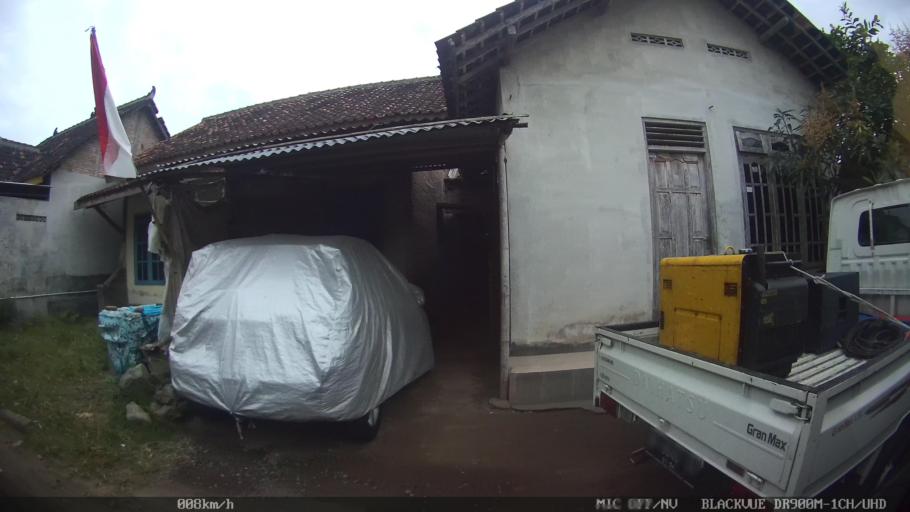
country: ID
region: Daerah Istimewa Yogyakarta
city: Sewon
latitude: -7.8328
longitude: 110.4081
